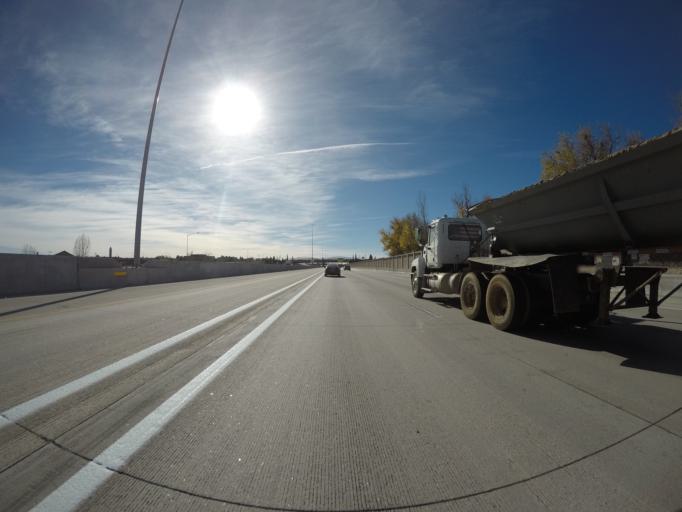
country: US
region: Colorado
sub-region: Adams County
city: Westminster
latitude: 39.8666
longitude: -105.0580
